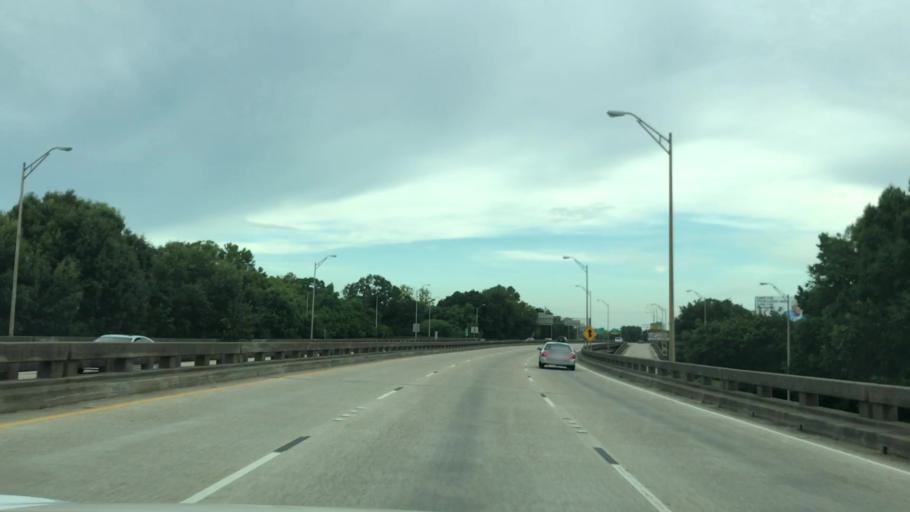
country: US
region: Louisiana
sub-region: East Baton Rouge Parish
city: Baton Rouge
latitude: 30.4816
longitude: -91.1663
